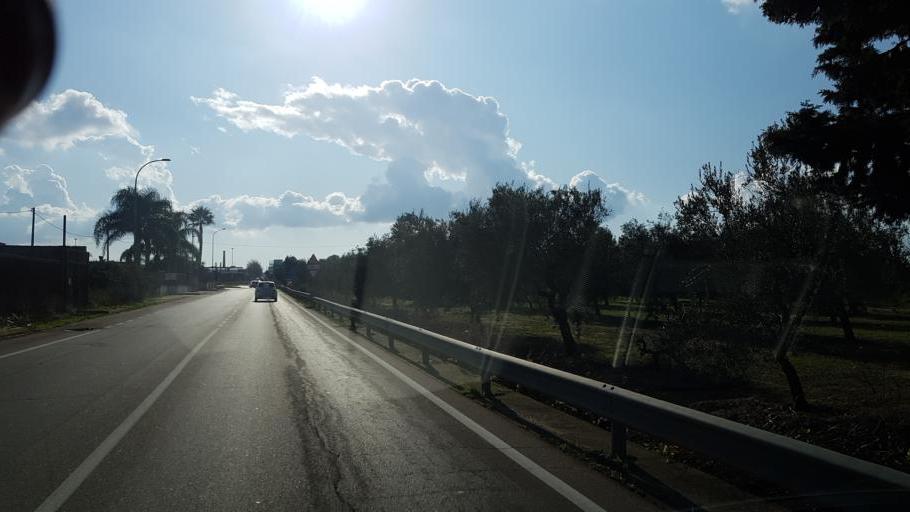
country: IT
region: Apulia
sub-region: Provincia di Lecce
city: Salice Salentino
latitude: 40.3926
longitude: 17.9684
